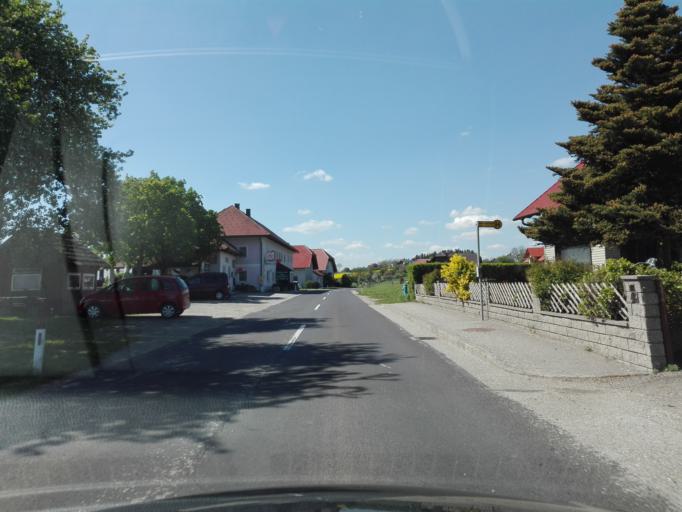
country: AT
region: Upper Austria
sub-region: Politischer Bezirk Urfahr-Umgebung
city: Feldkirchen an der Donau
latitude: 48.3471
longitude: 13.9480
